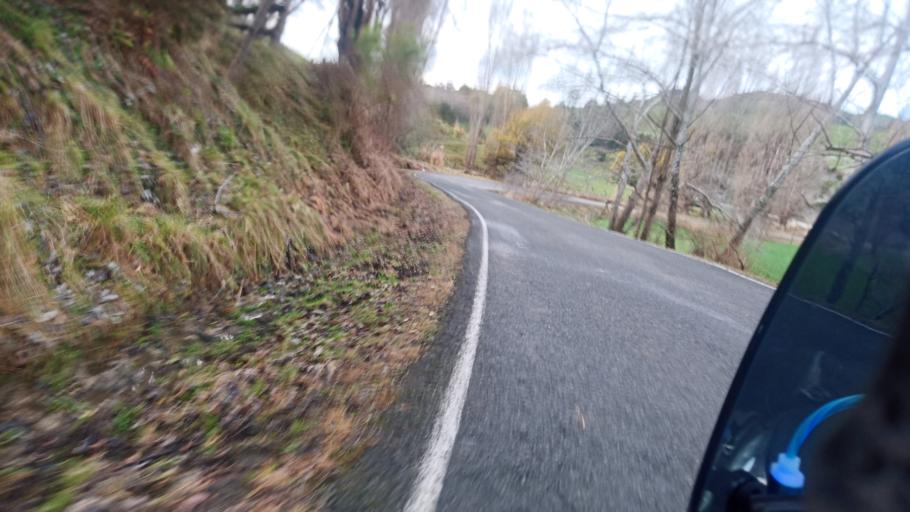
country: NZ
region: Gisborne
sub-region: Gisborne District
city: Gisborne
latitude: -38.4289
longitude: 177.9159
